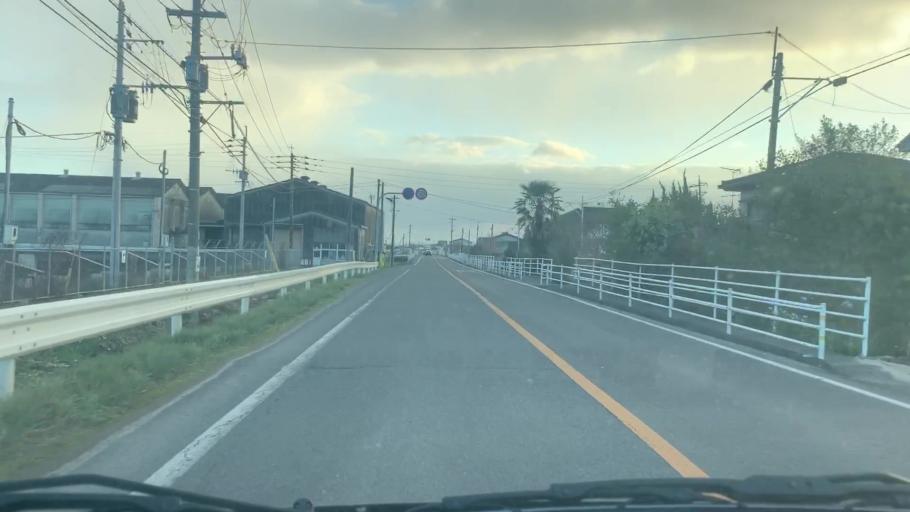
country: JP
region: Saga Prefecture
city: Saga-shi
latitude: 33.1926
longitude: 130.1929
